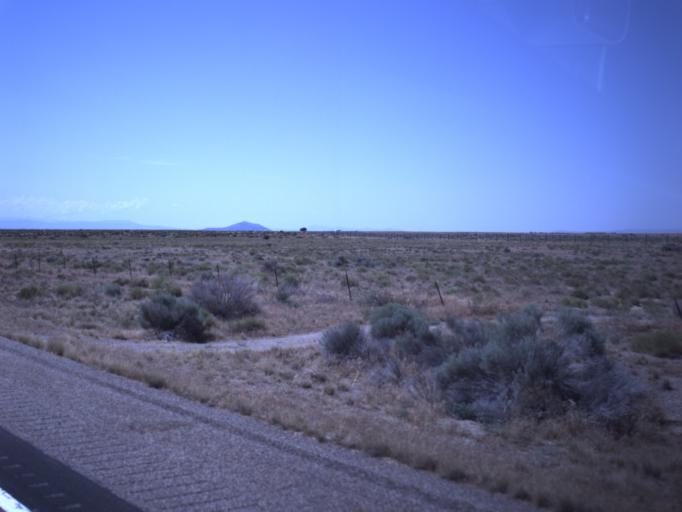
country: US
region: Utah
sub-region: Millard County
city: Delta
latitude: 39.3897
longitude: -112.4995
